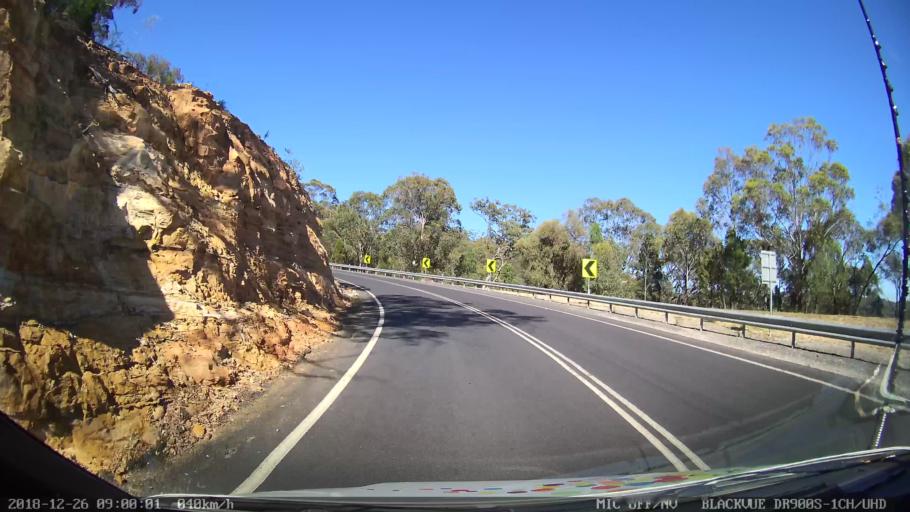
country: AU
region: New South Wales
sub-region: Mid-Western Regional
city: Kandos
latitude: -32.6341
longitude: 150.0362
